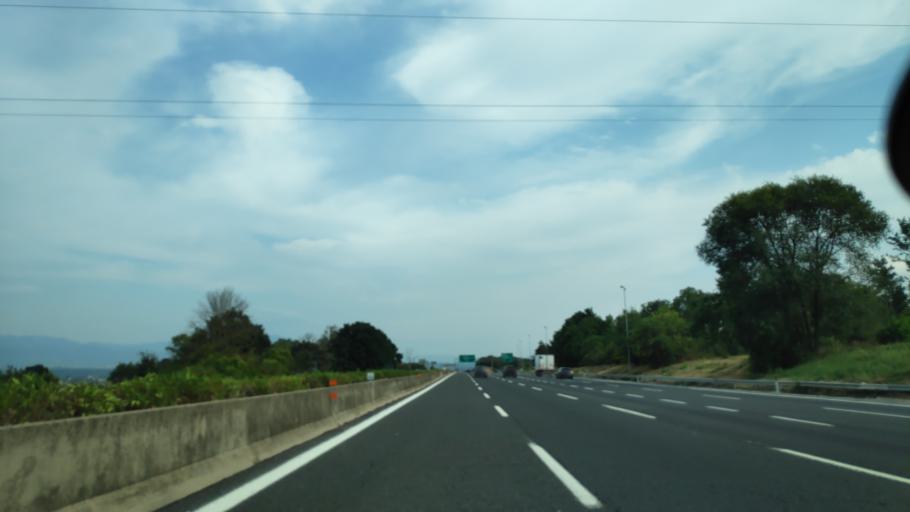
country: IT
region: Latium
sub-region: Citta metropolitana di Roma Capitale
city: Fiano Romano
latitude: 42.1695
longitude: 12.6119
